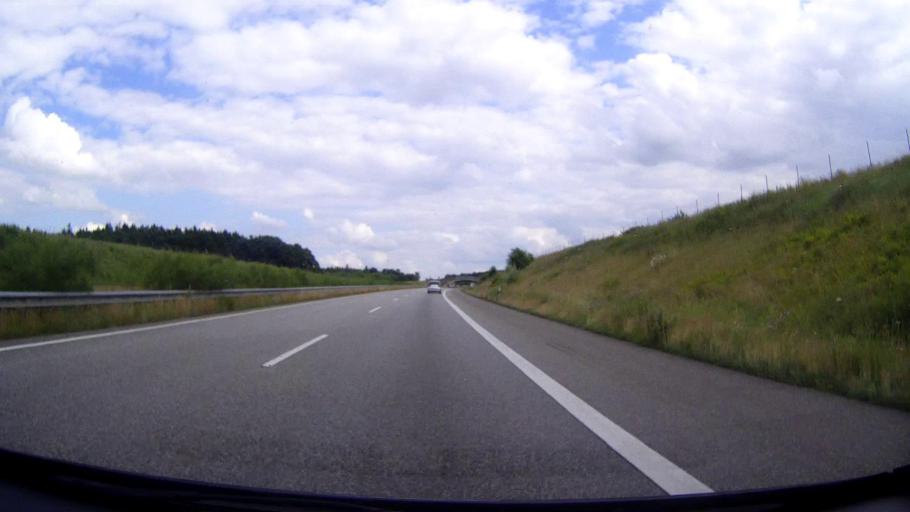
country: DE
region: Schleswig-Holstein
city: Strukdorf
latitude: 53.9222
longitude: 10.4940
